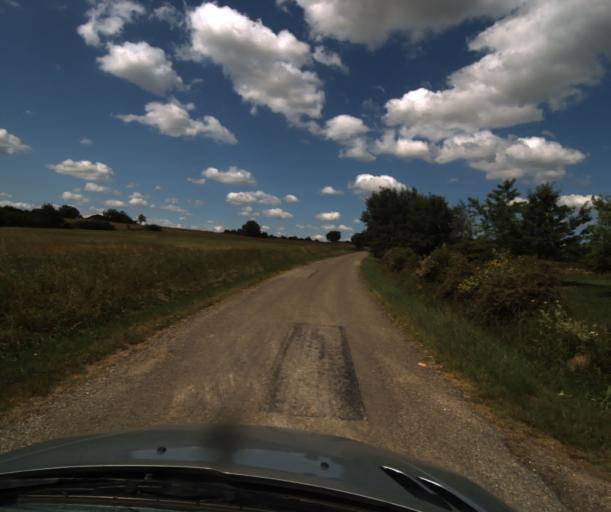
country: FR
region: Midi-Pyrenees
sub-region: Departement du Tarn-et-Garonne
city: Campsas
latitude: 43.9168
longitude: 1.2937
